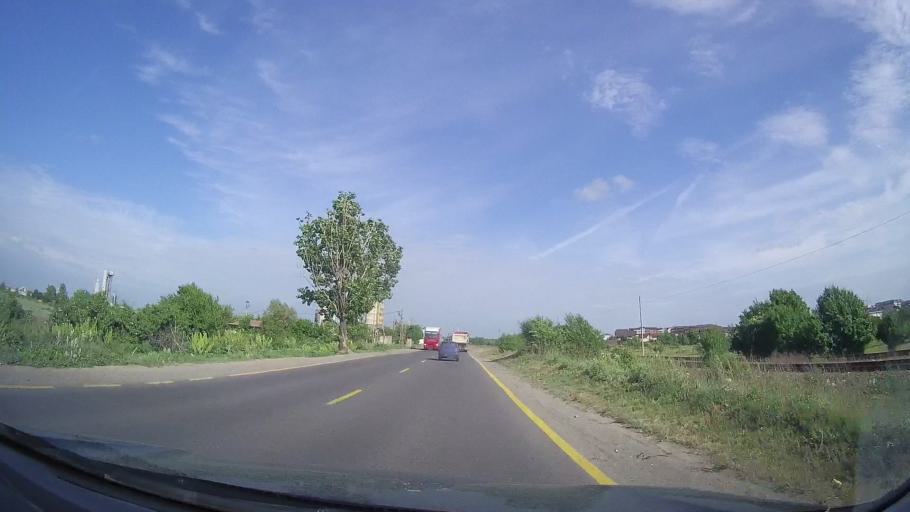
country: RO
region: Ilfov
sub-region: Comuna Magurele
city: Varteju
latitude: 44.3772
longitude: 26.0029
